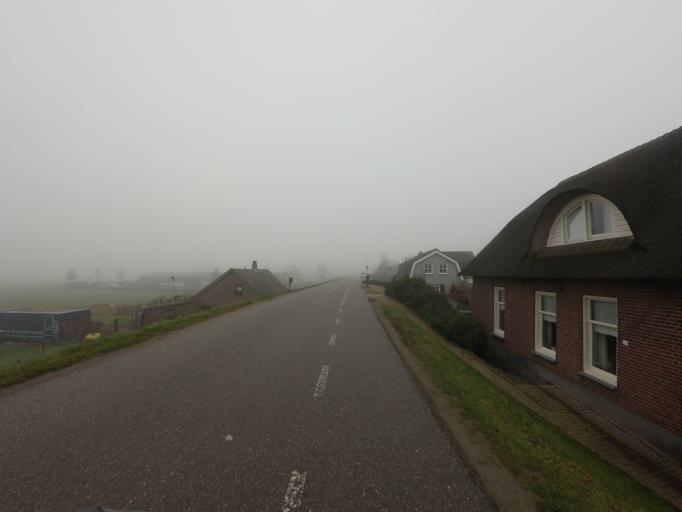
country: NL
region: Gelderland
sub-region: Gemeente Zaltbommel
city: Nederhemert
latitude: 51.7643
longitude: 5.1512
